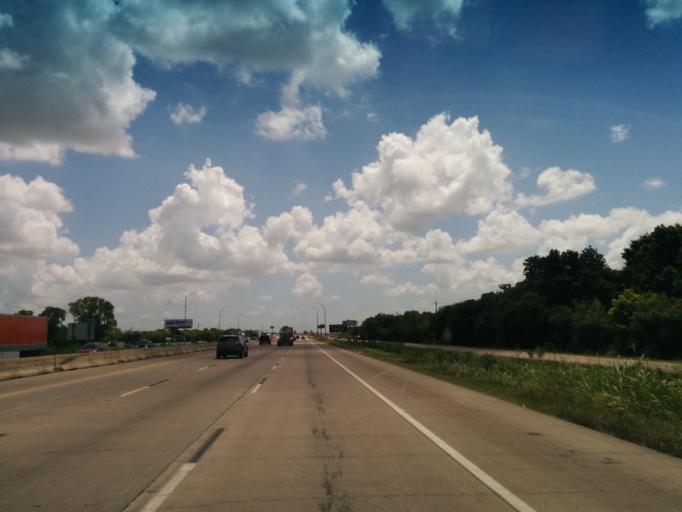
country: US
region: Texas
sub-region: Harris County
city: Baytown
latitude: 29.8061
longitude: -94.9738
